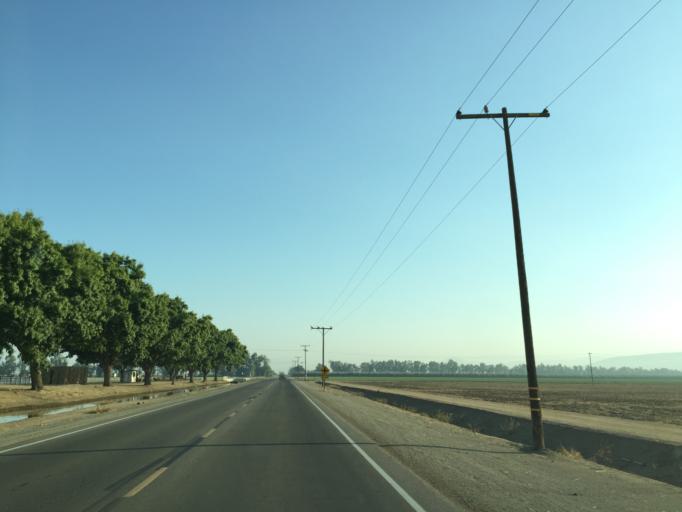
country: US
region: California
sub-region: Tulare County
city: Cutler
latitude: 36.4557
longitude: -119.2776
